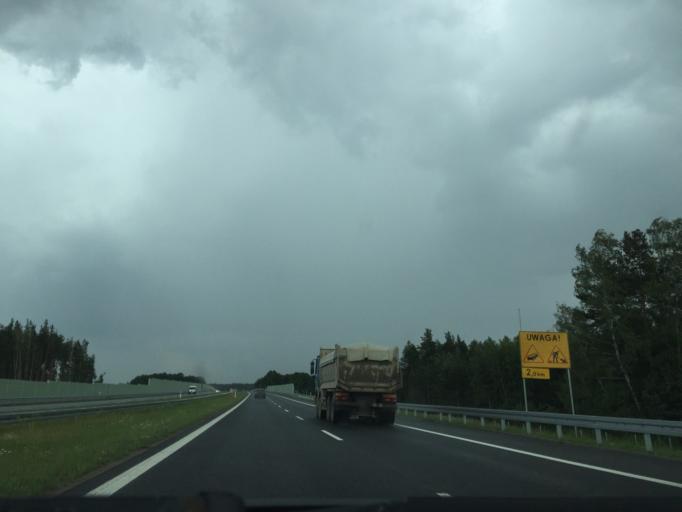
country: PL
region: Masovian Voivodeship
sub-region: Powiat szydlowiecki
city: Oronsko
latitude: 51.3071
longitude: 21.0047
